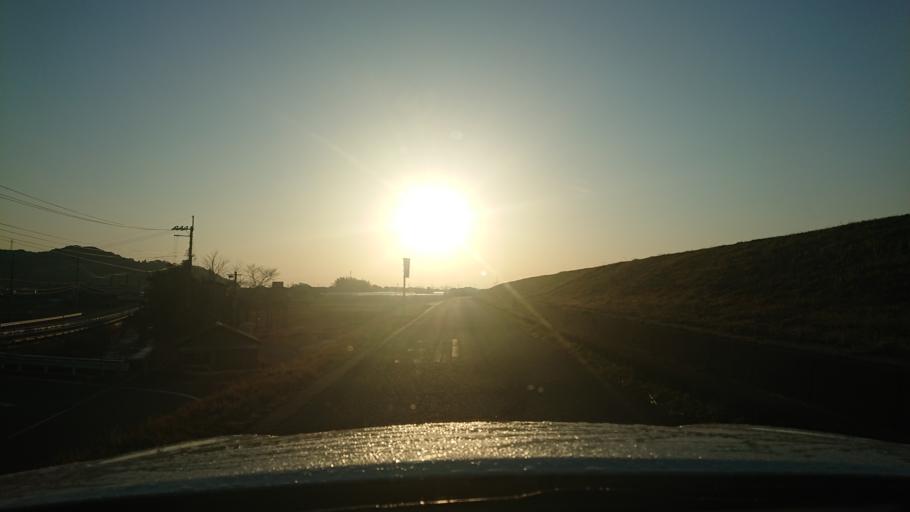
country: JP
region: Tokushima
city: Komatsushimacho
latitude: 33.9432
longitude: 134.5895
